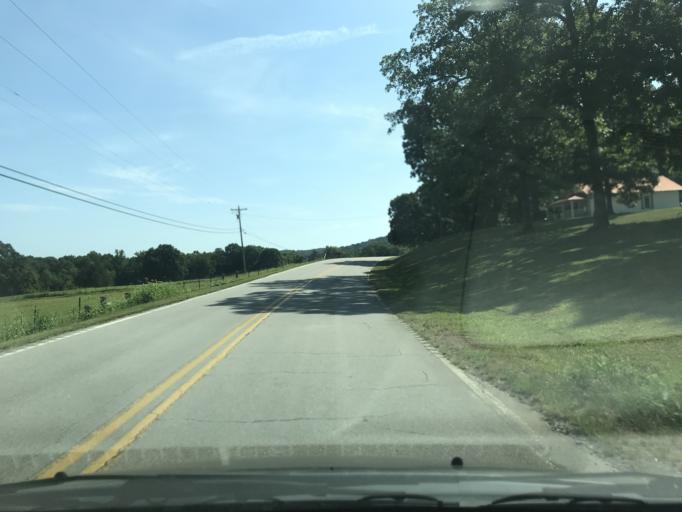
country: US
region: Tennessee
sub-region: Hamilton County
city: Sale Creek
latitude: 35.3288
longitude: -85.0146
